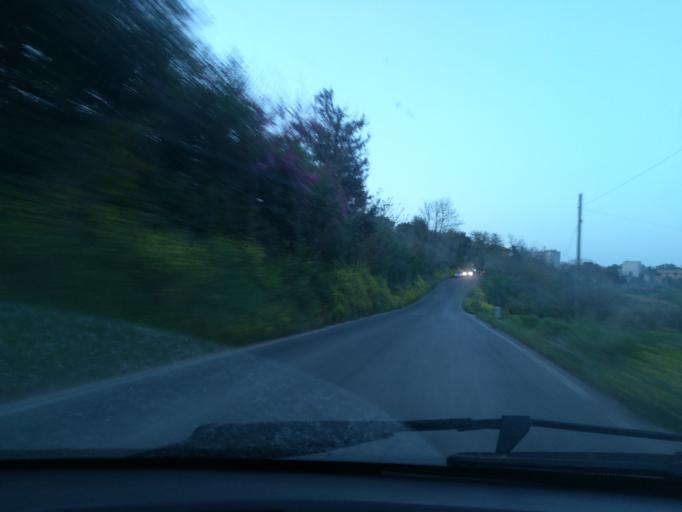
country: IT
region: The Marches
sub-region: Provincia di Macerata
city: Macerata
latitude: 43.2846
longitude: 13.4502
